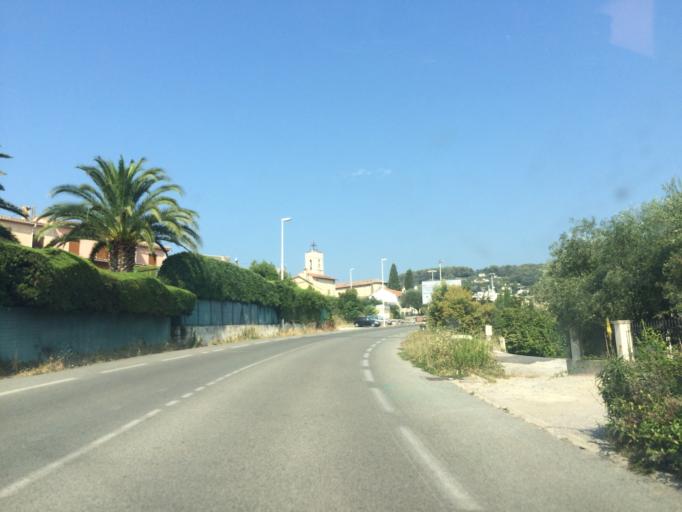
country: FR
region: Provence-Alpes-Cote d'Azur
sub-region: Departement des Alpes-Maritimes
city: La Colle-sur-Loup
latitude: 43.6864
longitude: 7.1079
